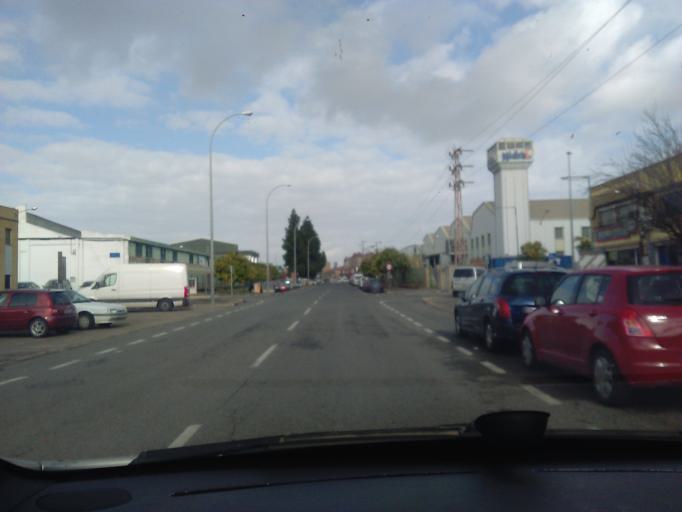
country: ES
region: Andalusia
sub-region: Provincia de Sevilla
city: Sevilla
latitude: 37.3799
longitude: -5.9249
